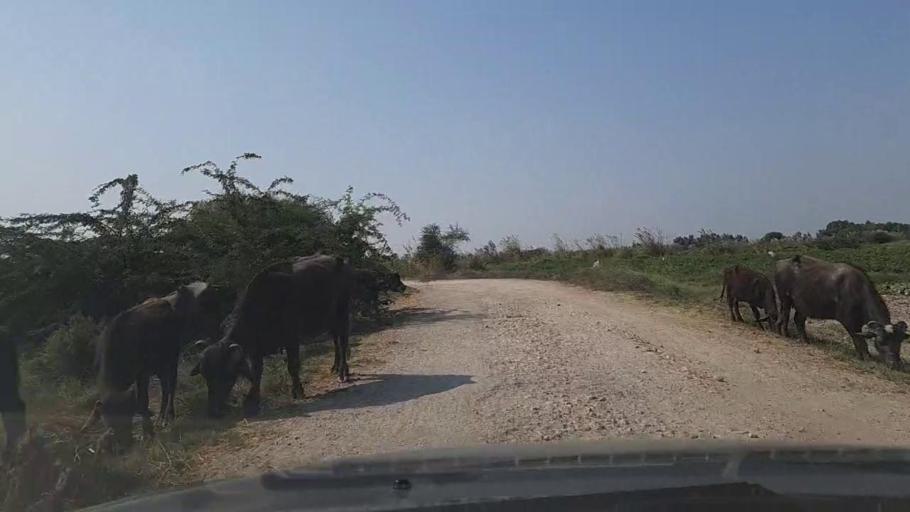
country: PK
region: Sindh
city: Mirpur Sakro
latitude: 24.4030
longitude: 67.6686
